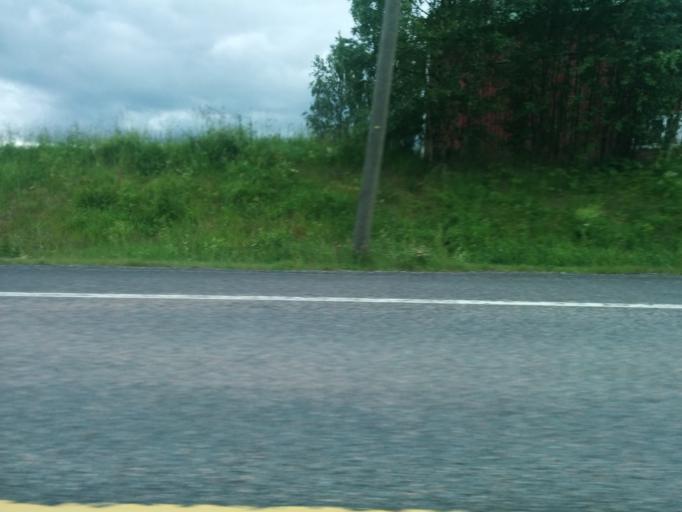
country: FI
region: Pirkanmaa
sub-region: Tampere
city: Orivesi
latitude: 61.6903
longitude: 24.4030
